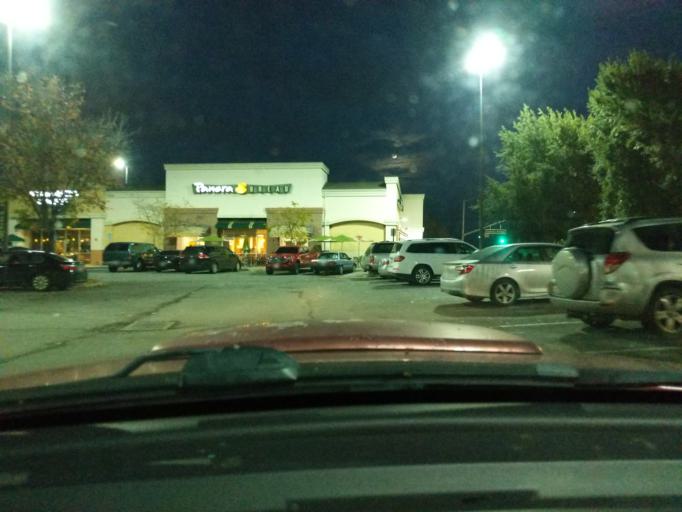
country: US
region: California
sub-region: Santa Clara County
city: Gilroy
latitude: 37.0021
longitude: -121.5517
